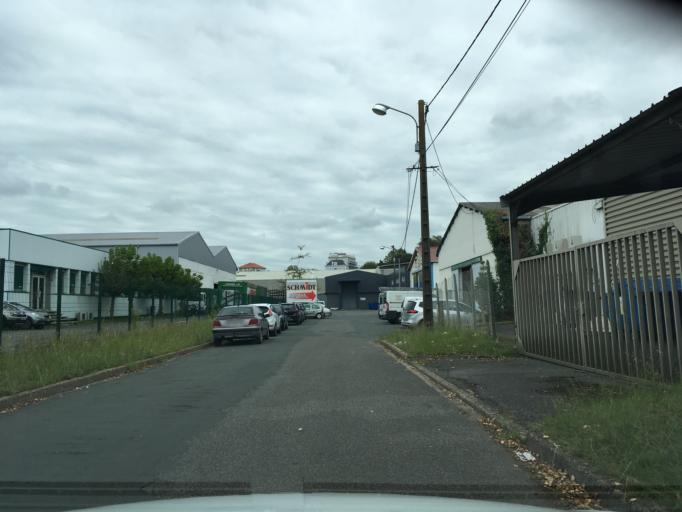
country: FR
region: Aquitaine
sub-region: Departement des Pyrenees-Atlantiques
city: Bayonne
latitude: 43.4945
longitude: -1.4943
